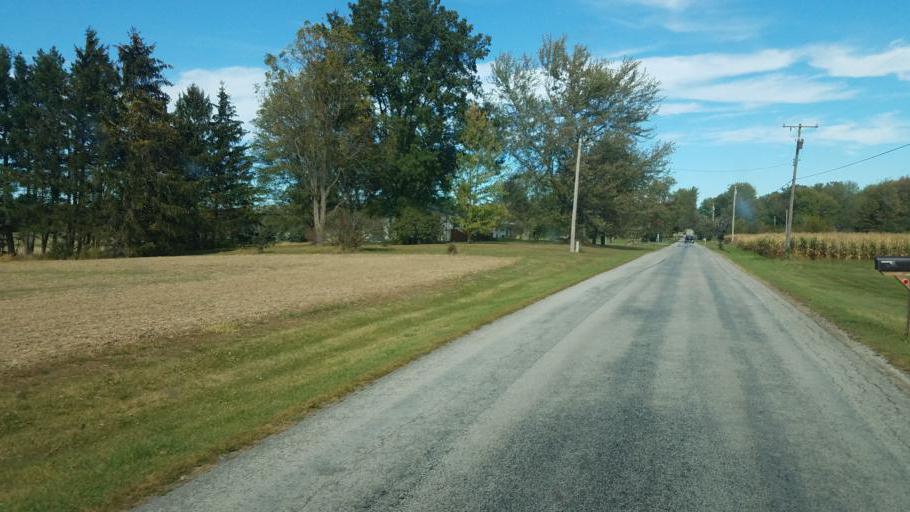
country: US
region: Ohio
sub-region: Huron County
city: Wakeman
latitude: 41.2373
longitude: -82.4667
